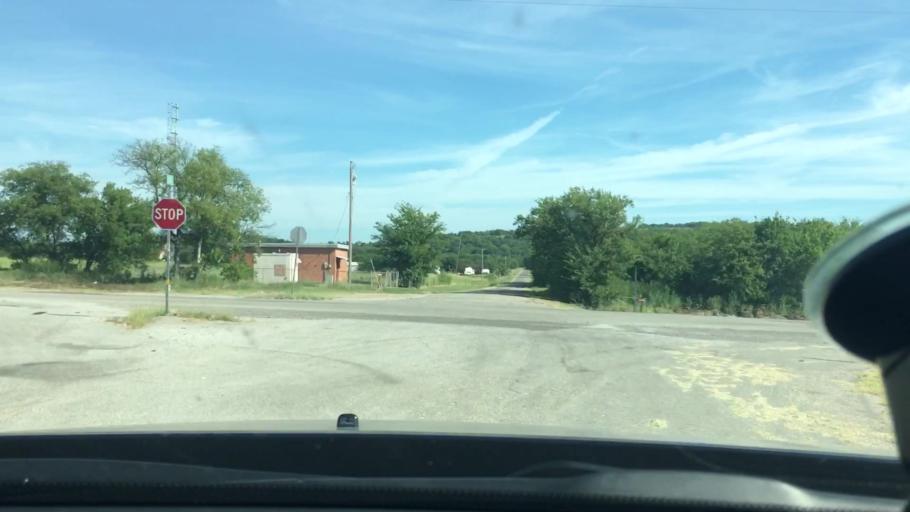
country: US
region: Oklahoma
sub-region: Carter County
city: Lone Grove
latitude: 34.3324
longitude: -97.2825
